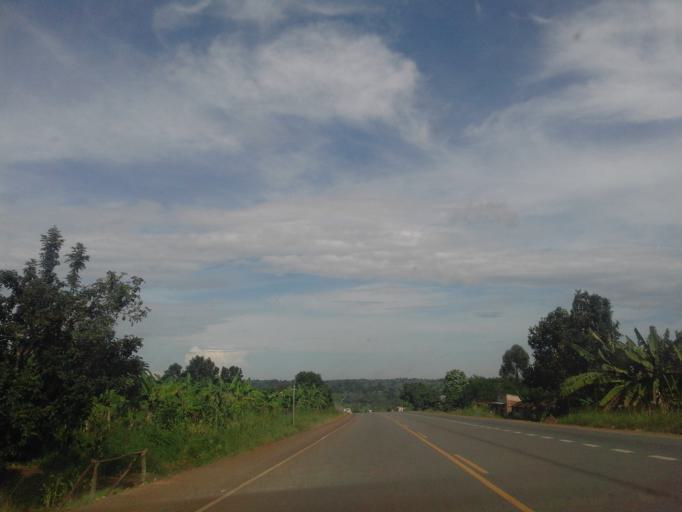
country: UG
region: Central Region
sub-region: Lwengo District
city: Lwengo
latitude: -0.3738
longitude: 31.5192
